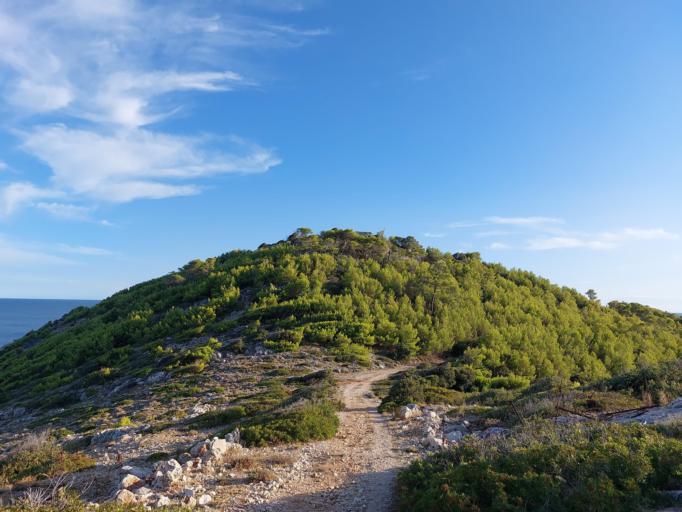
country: HR
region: Dubrovacko-Neretvanska
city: Smokvica
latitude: 42.7269
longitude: 16.8450
